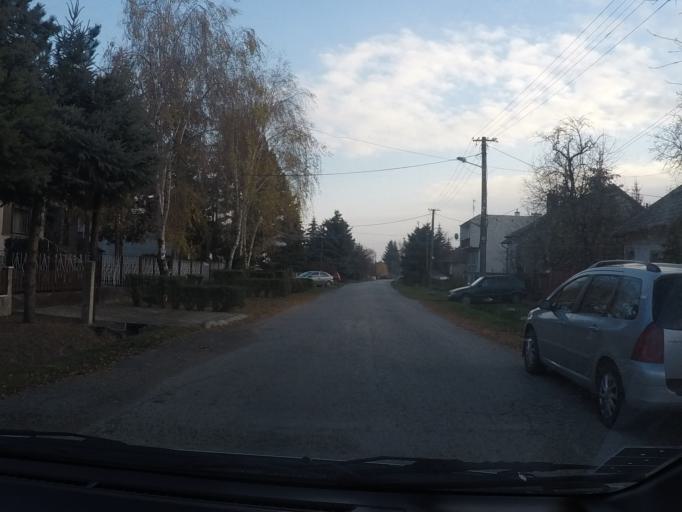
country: SK
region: Nitriansky
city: Levice
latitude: 48.1108
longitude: 18.5287
